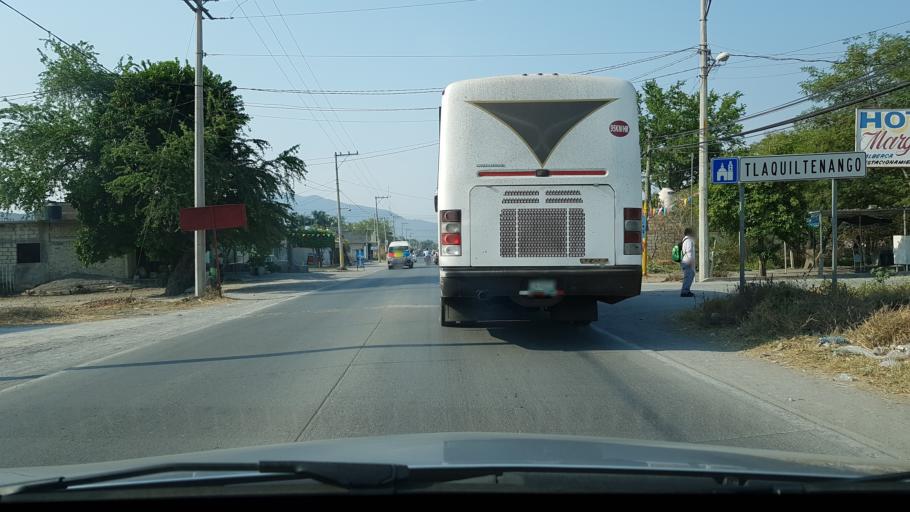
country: MX
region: Morelos
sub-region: Tlaquiltenango
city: Alfredo V. Bonfil (Chacampalco)
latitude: 18.6484
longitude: -99.1559
